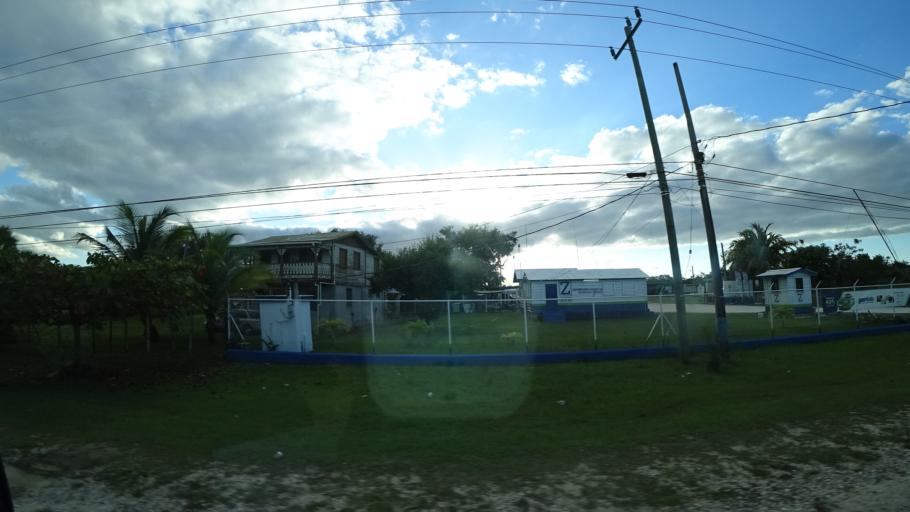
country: BZ
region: Belize
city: Belize City
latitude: 17.5803
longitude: -88.3440
